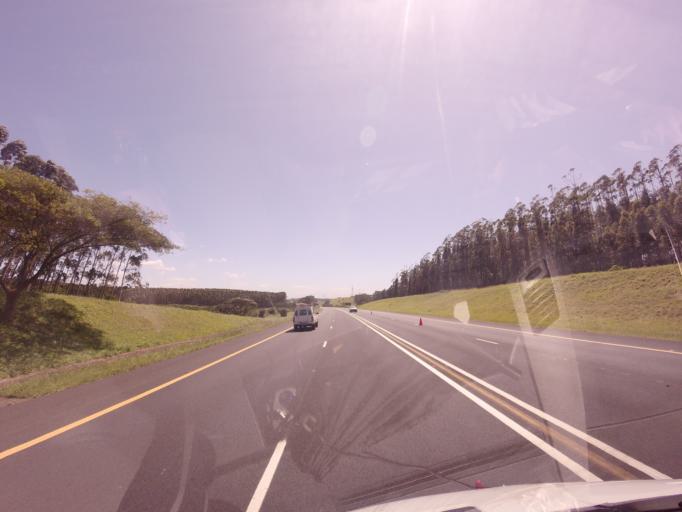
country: ZA
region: KwaZulu-Natal
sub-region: uThungulu District Municipality
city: eSikhawini
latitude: -28.9757
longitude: 31.7242
